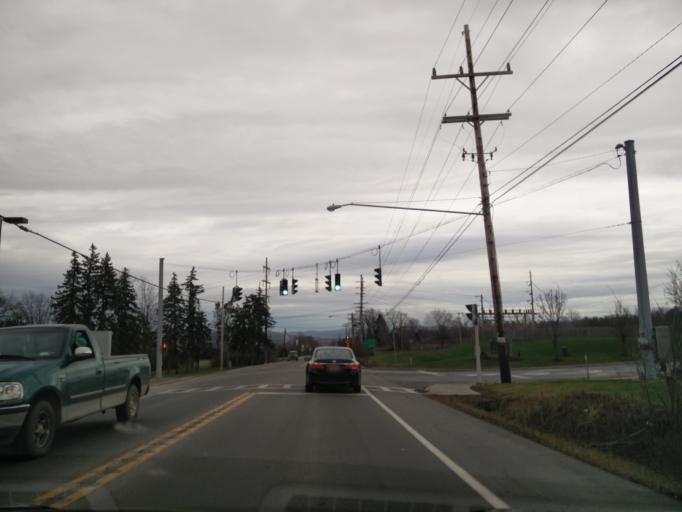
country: US
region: New York
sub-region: Tompkins County
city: Northwest Ithaca
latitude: 42.4667
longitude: -76.5399
